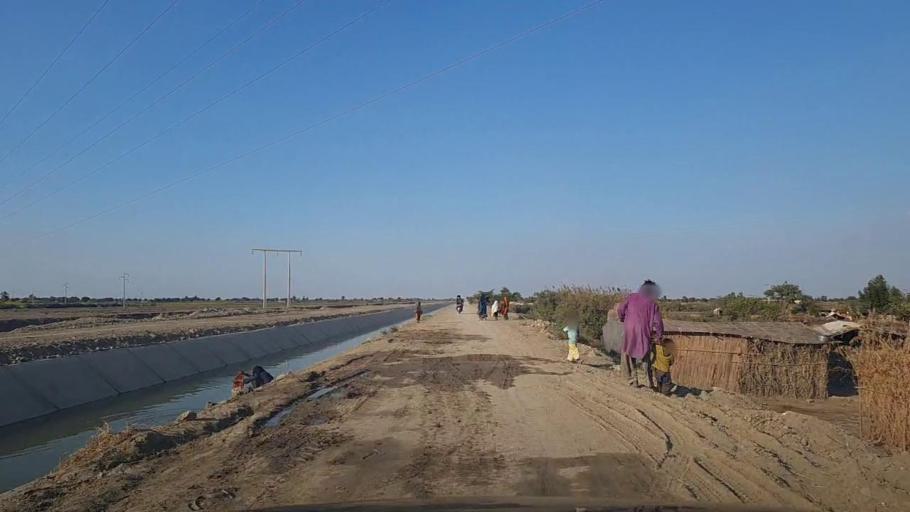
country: PK
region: Sindh
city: Jhol
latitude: 25.8841
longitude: 69.0374
